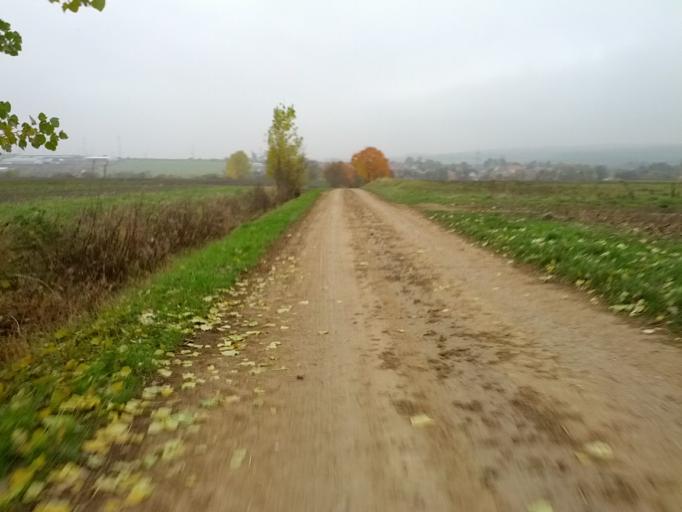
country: DE
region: Thuringia
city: Seebach
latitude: 50.9844
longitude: 10.4072
